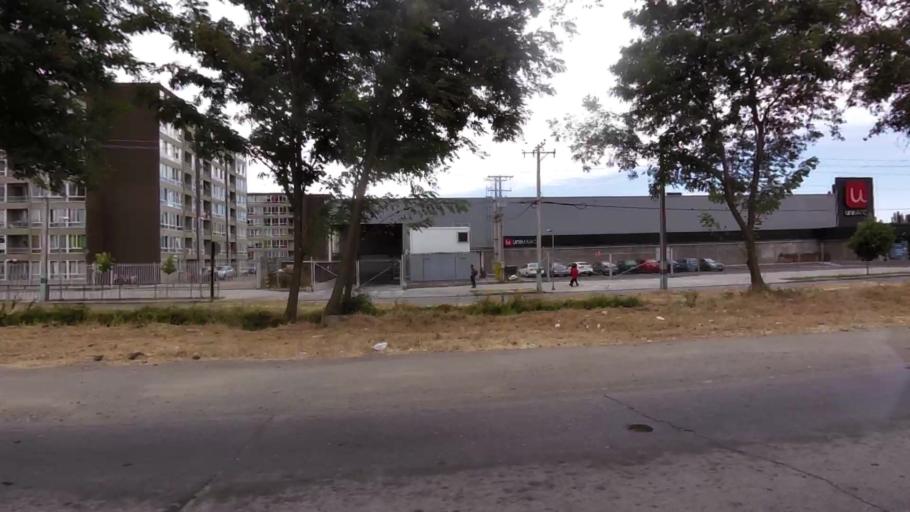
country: CL
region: O'Higgins
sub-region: Provincia de Cachapoal
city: Rancagua
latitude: -34.1405
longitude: -70.7364
